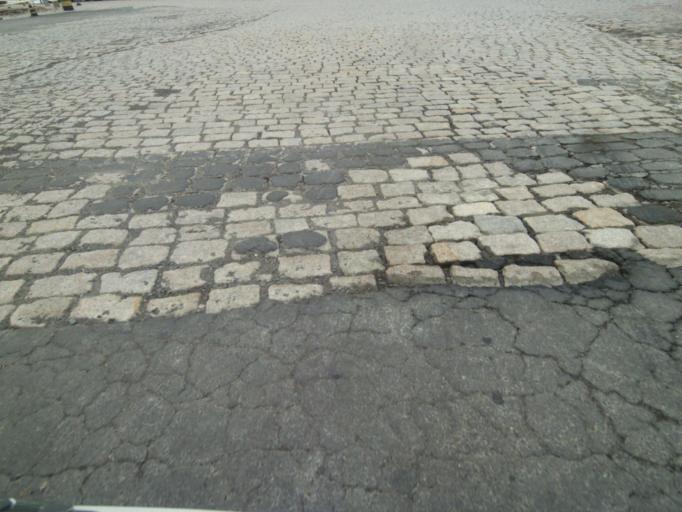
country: BR
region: Parana
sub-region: Campo Largo
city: Campo Largo
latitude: -25.4644
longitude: -49.7345
